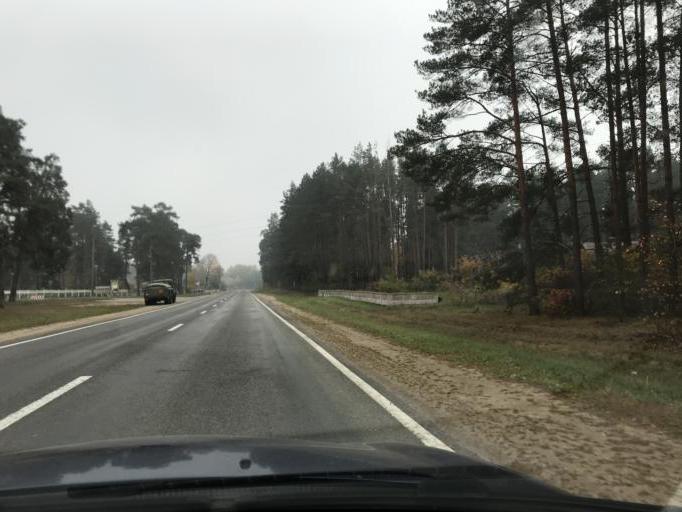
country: BY
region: Grodnenskaya
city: Hrodna
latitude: 53.8408
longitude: 23.8939
